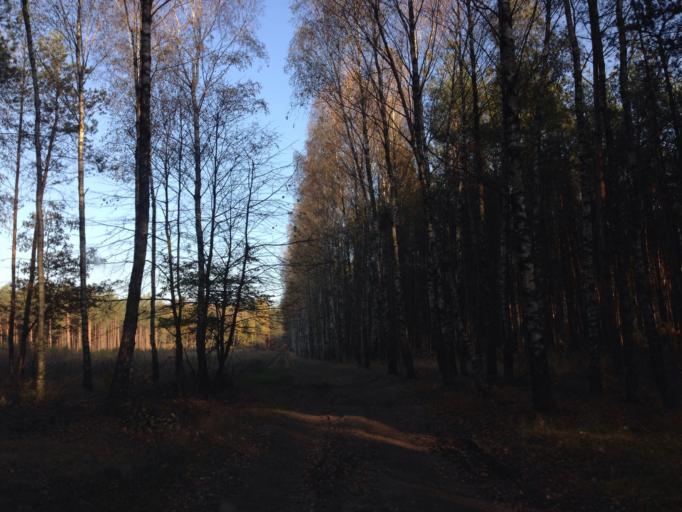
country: PL
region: Kujawsko-Pomorskie
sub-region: Powiat brodnicki
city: Gorzno
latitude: 53.1596
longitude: 19.6642
